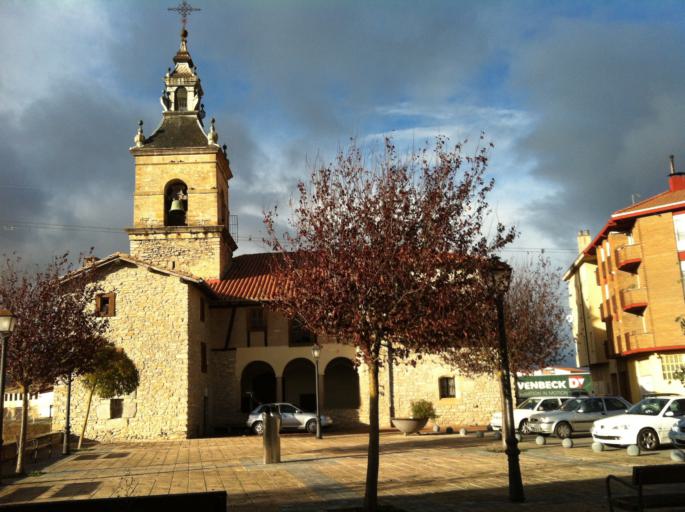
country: ES
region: Basque Country
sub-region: Provincia de Alava
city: Gasteiz / Vitoria
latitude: 42.8613
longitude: -2.7315
